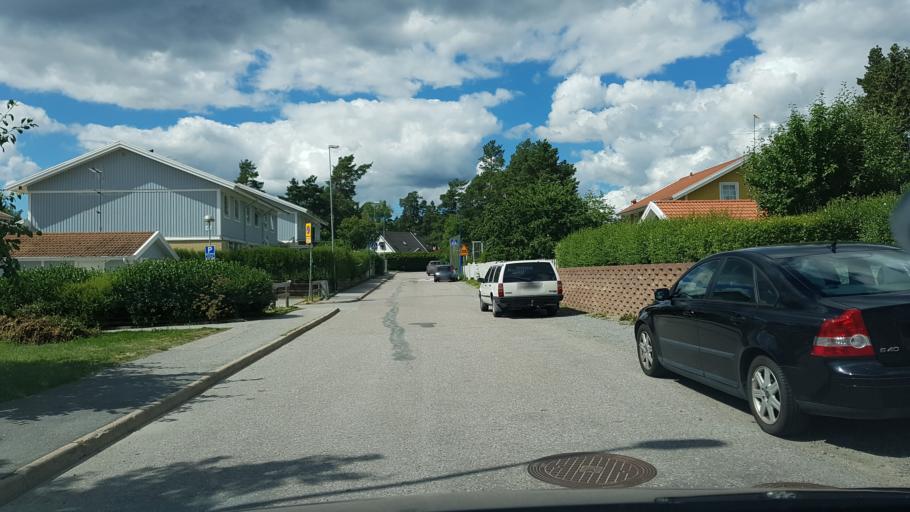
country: SE
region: Stockholm
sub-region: Upplands-Bro Kommun
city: Kungsaengen
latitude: 59.4784
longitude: 17.8059
